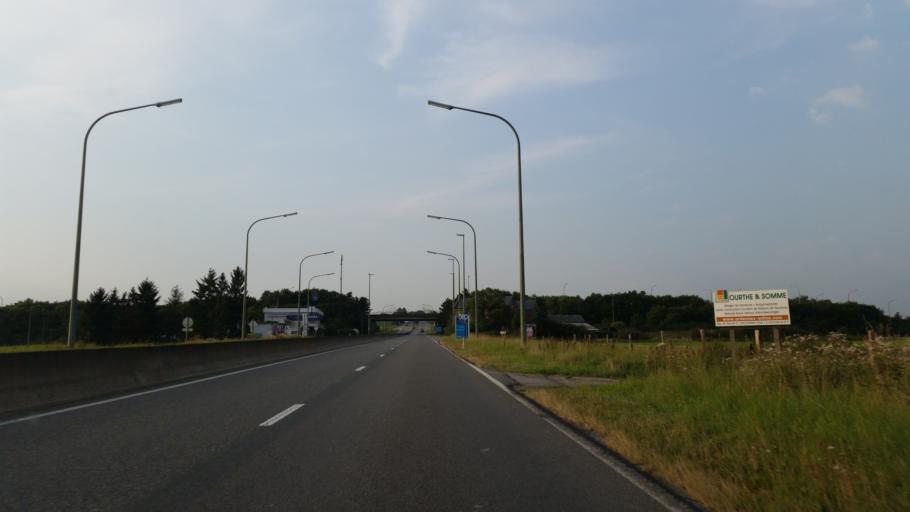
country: BE
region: Wallonia
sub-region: Province de Namur
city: Somme-Leuze
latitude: 50.2883
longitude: 5.3490
